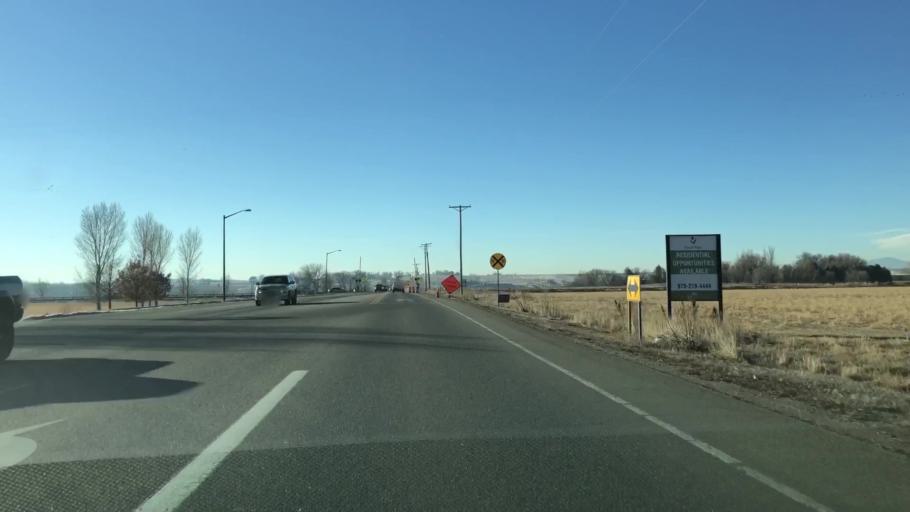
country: US
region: Colorado
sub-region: Larimer County
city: Loveland
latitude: 40.4017
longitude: -105.0212
